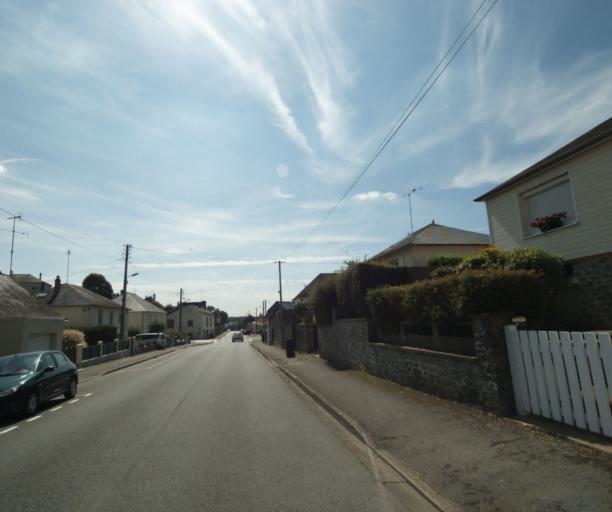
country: FR
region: Pays de la Loire
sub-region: Departement de la Mayenne
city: Laval
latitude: 48.0620
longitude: -0.7708
